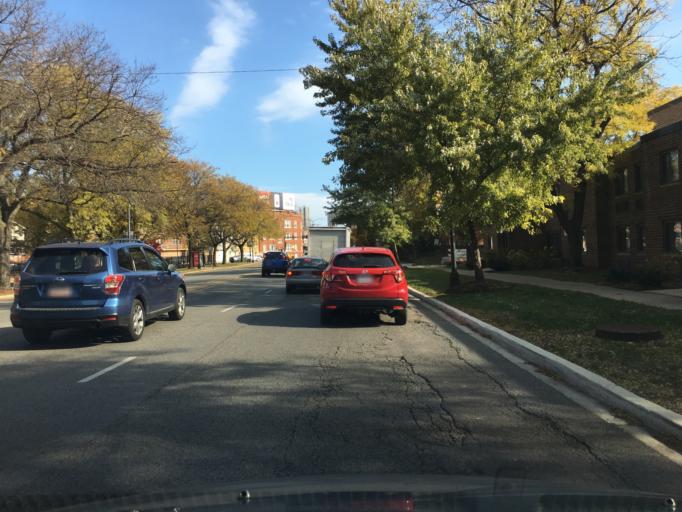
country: US
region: Illinois
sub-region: Cook County
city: Evanston
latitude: 41.9907
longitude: -87.6739
